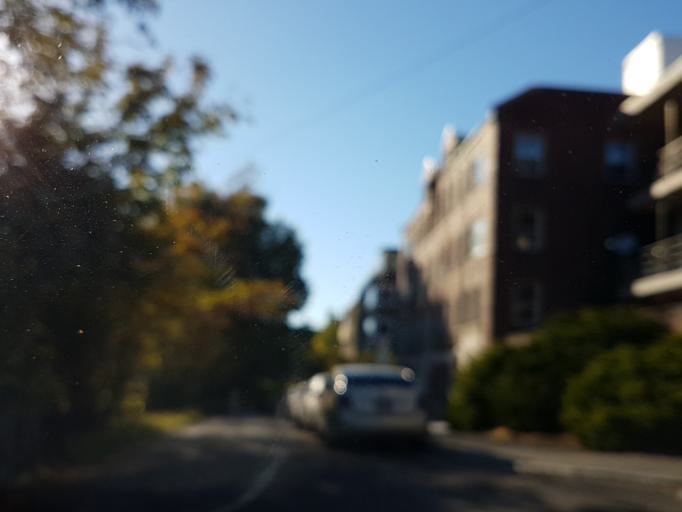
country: US
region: Washington
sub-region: King County
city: Seattle
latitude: 47.6264
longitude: -122.3553
